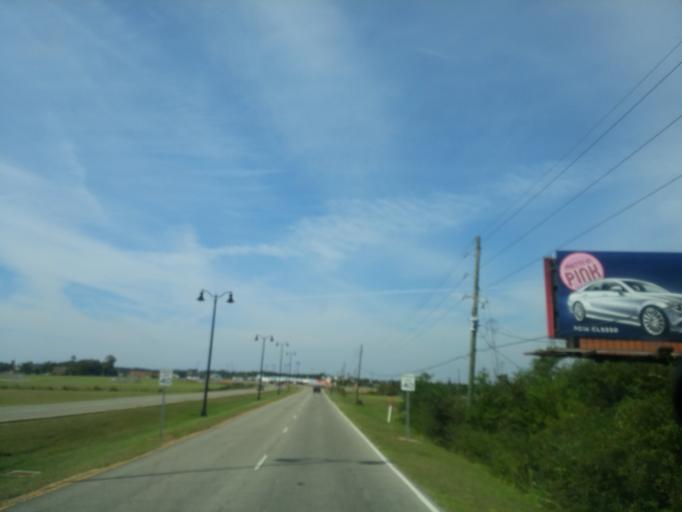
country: US
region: Mississippi
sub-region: Harrison County
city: West Gulfport
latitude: 30.4195
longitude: -89.0841
